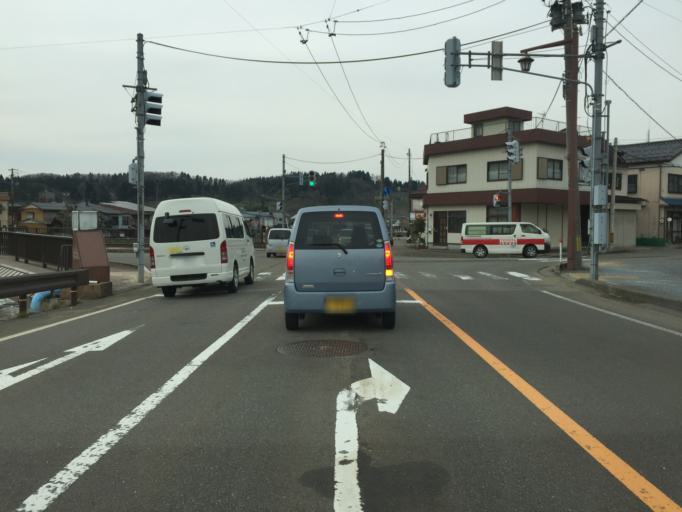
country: JP
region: Niigata
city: Tochio-honcho
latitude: 37.4781
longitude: 138.9968
